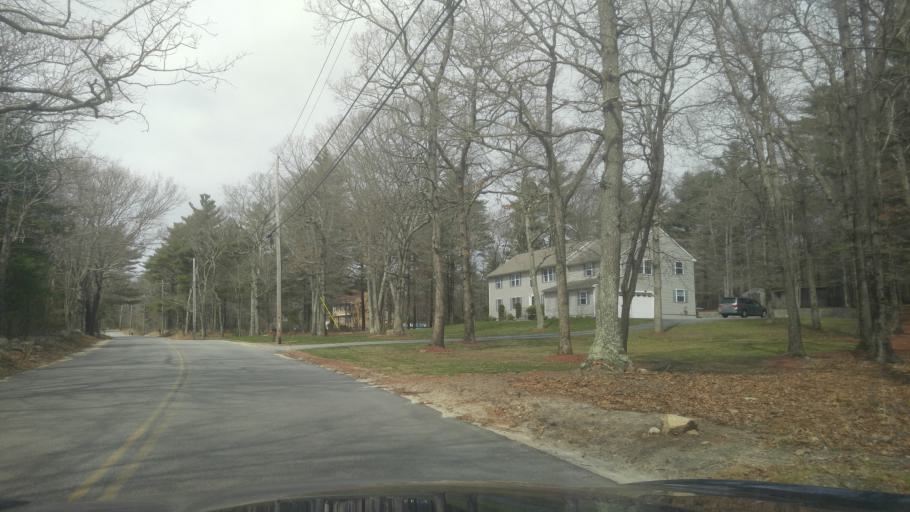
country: US
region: Rhode Island
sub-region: Washington County
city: Exeter
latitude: 41.6206
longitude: -71.5638
